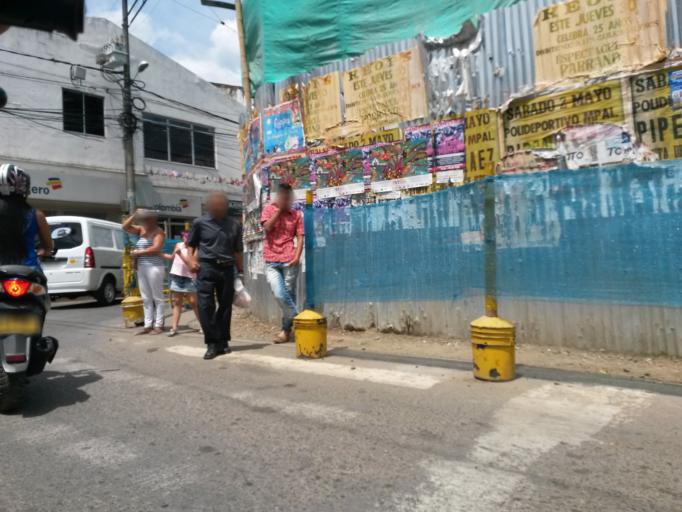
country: CO
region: Cauca
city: Santander de Quilichao
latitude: 3.0072
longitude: -76.4830
